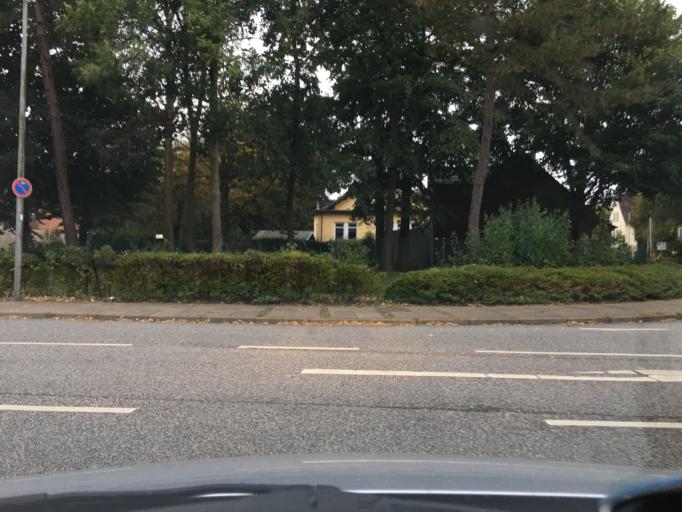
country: DE
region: Schleswig-Holstein
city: Eckernforde
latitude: 54.4661
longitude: 9.8391
